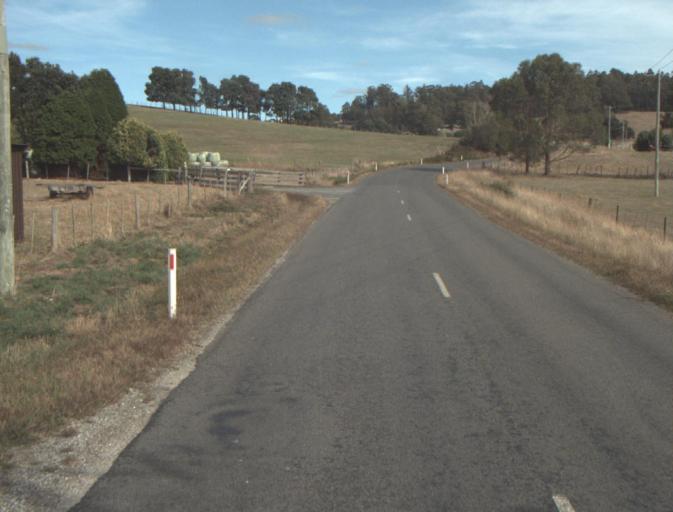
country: AU
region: Tasmania
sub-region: Launceston
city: Mayfield
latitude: -41.1944
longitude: 147.2208
